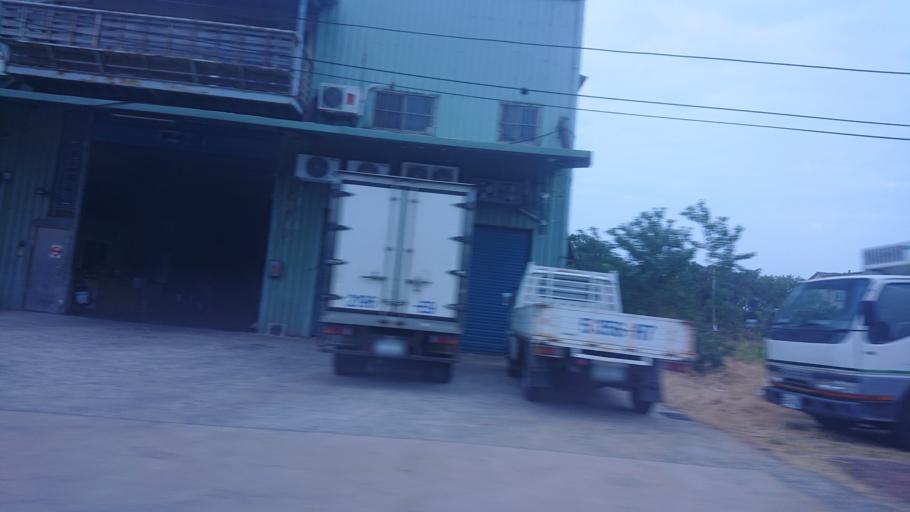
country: TW
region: Fukien
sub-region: Kinmen
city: Jincheng
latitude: 24.4387
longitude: 118.3119
